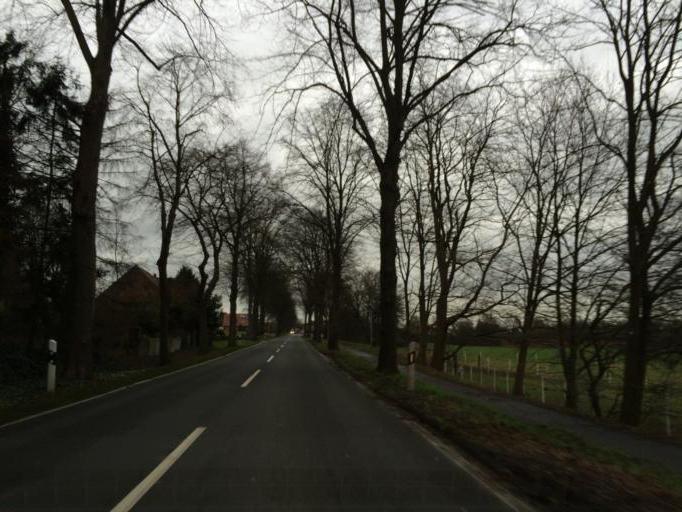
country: DE
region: North Rhine-Westphalia
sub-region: Regierungsbezirk Munster
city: Haltern
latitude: 51.7331
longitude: 7.1632
